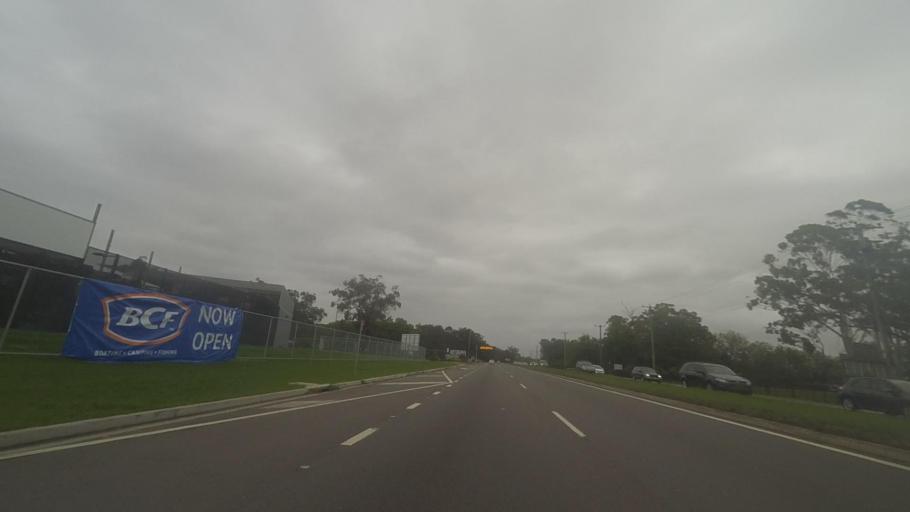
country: AU
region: New South Wales
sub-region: Port Stephens Shire
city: Raymond Terrace
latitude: -32.7924
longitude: 151.7241
